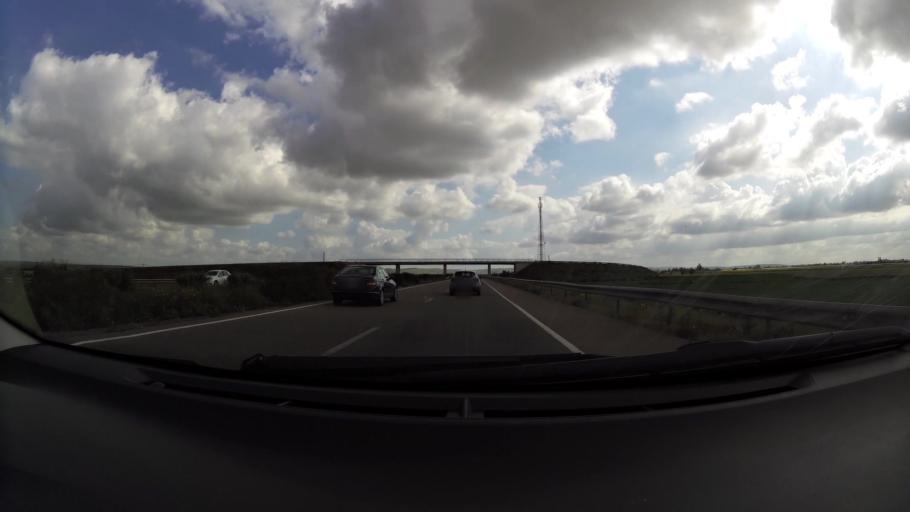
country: MA
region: Chaouia-Ouardigha
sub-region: Settat Province
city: Berrechid
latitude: 33.1370
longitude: -7.5767
